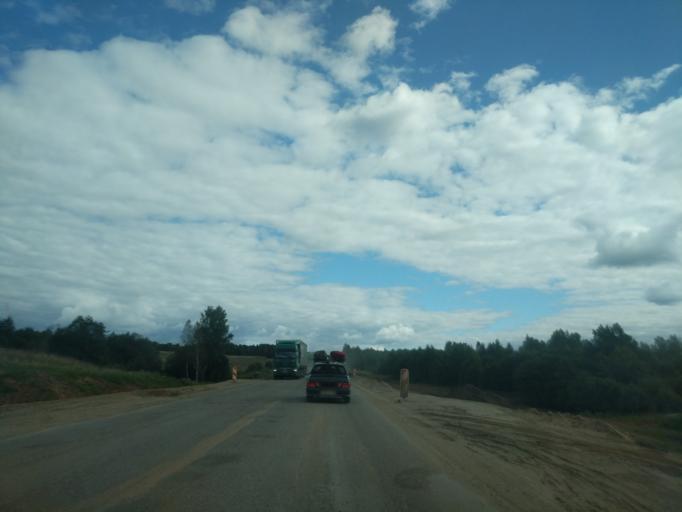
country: RU
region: Kostroma
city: Sudislavl'
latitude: 57.8735
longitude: 41.7383
